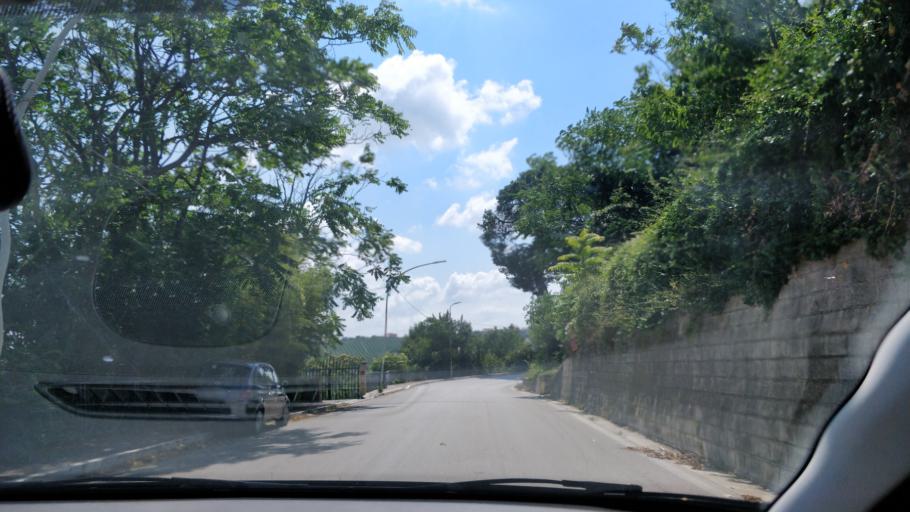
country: IT
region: Abruzzo
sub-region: Provincia di Chieti
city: Sambuceto
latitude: 42.4082
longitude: 14.2000
